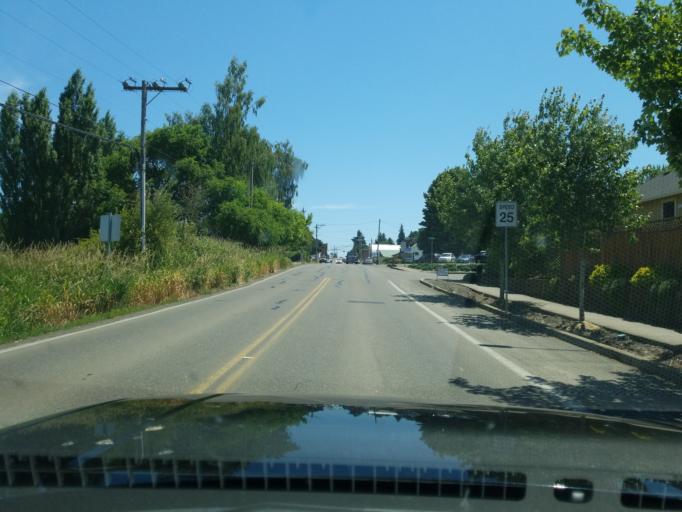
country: US
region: Oregon
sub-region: Yamhill County
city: Yamhill
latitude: 45.3415
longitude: -123.1917
